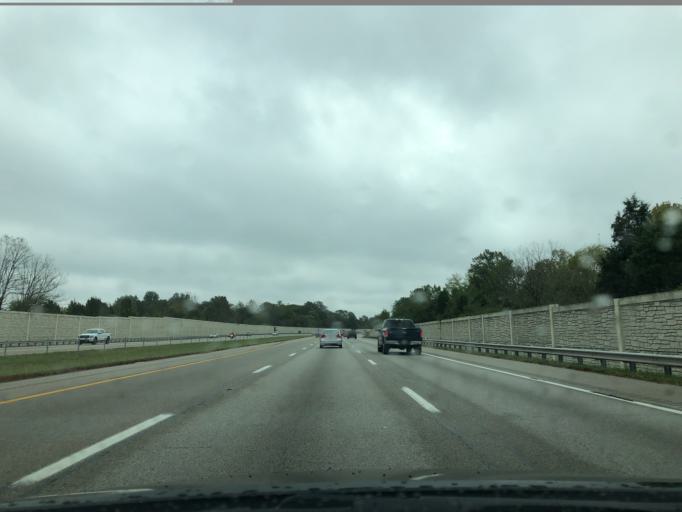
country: US
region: Ohio
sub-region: Hamilton County
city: The Village of Indian Hill
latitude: 39.2515
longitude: -84.3160
